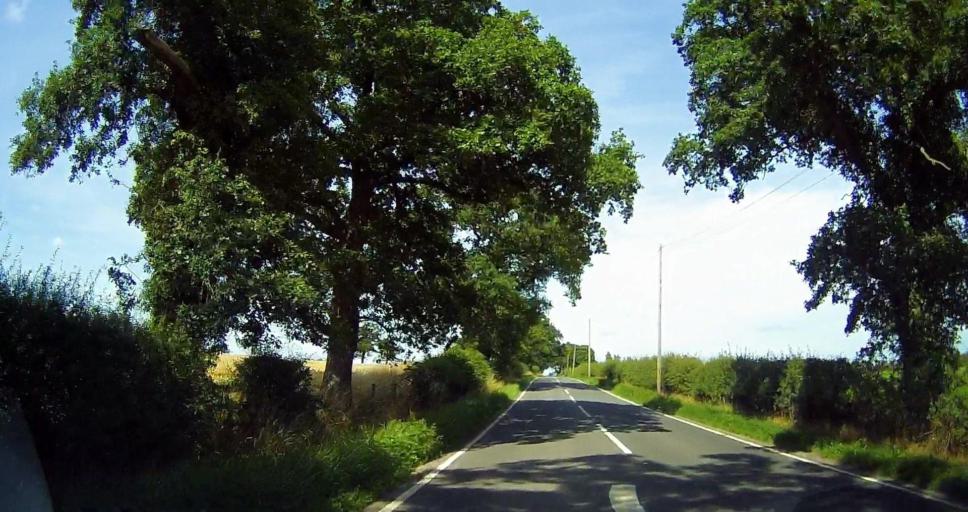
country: GB
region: England
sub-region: Shropshire
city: Market Drayton
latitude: 52.9394
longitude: -2.5048
